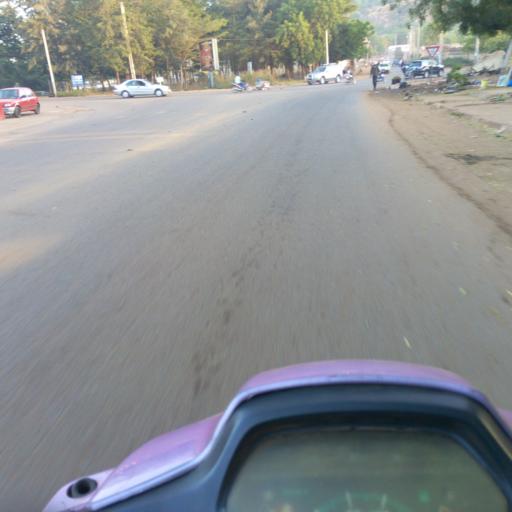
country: ML
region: Bamako
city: Bamako
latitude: 12.6535
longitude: -8.0129
